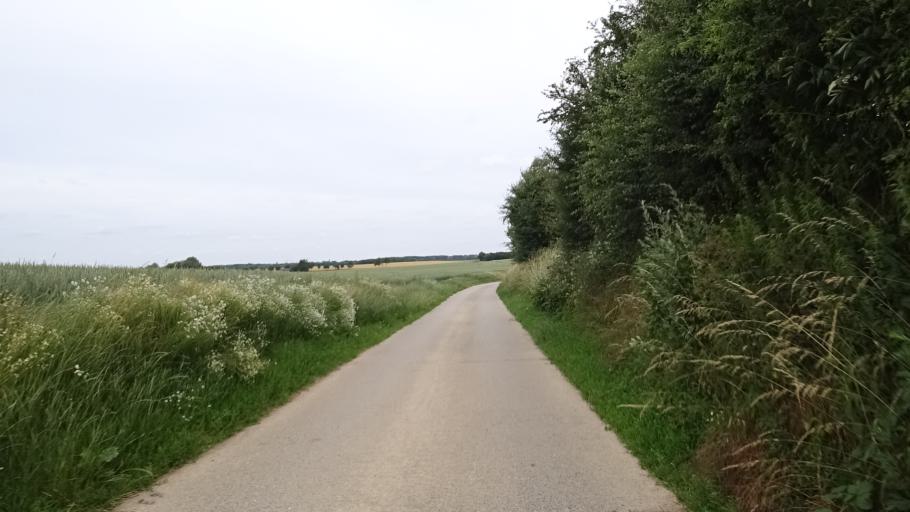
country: BE
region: Wallonia
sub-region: Province du Brabant Wallon
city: Walhain-Saint-Paul
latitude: 50.6476
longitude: 4.6708
